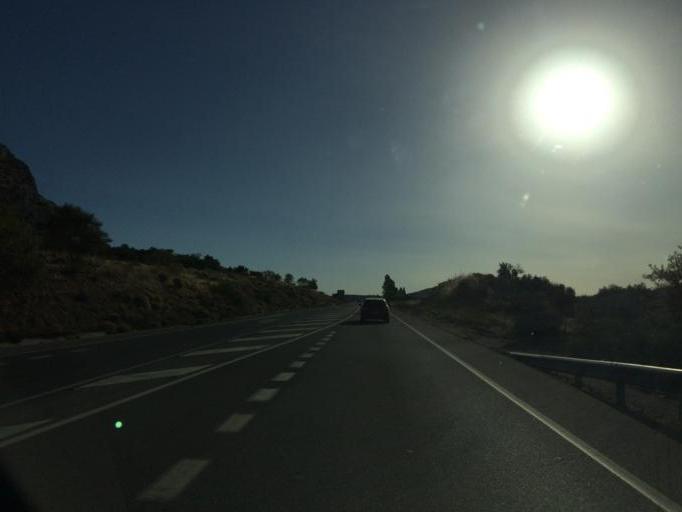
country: ES
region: Andalusia
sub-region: Provincia de Malaga
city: Teba
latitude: 36.9667
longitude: -4.8466
